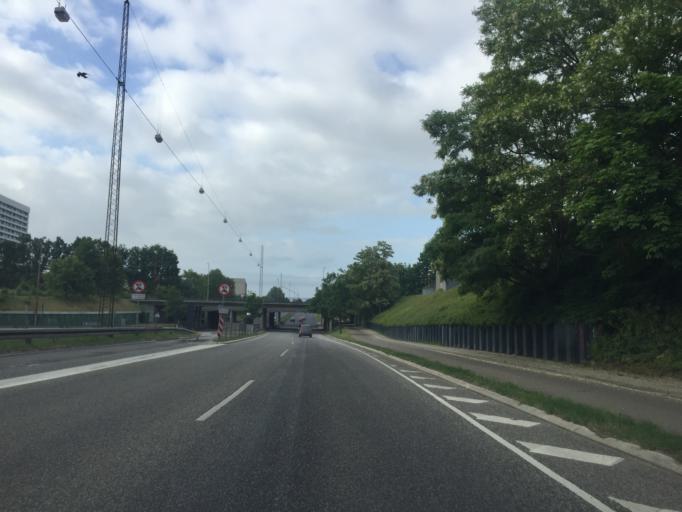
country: DK
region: Capital Region
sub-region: Rodovre Kommune
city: Rodovre
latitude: 55.6663
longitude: 12.4555
